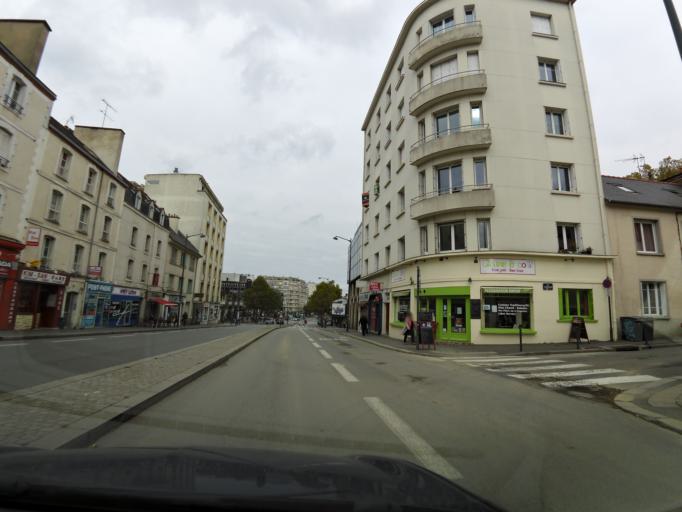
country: FR
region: Brittany
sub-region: Departement d'Ille-et-Vilaine
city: Rennes
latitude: 48.1038
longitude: -1.6770
